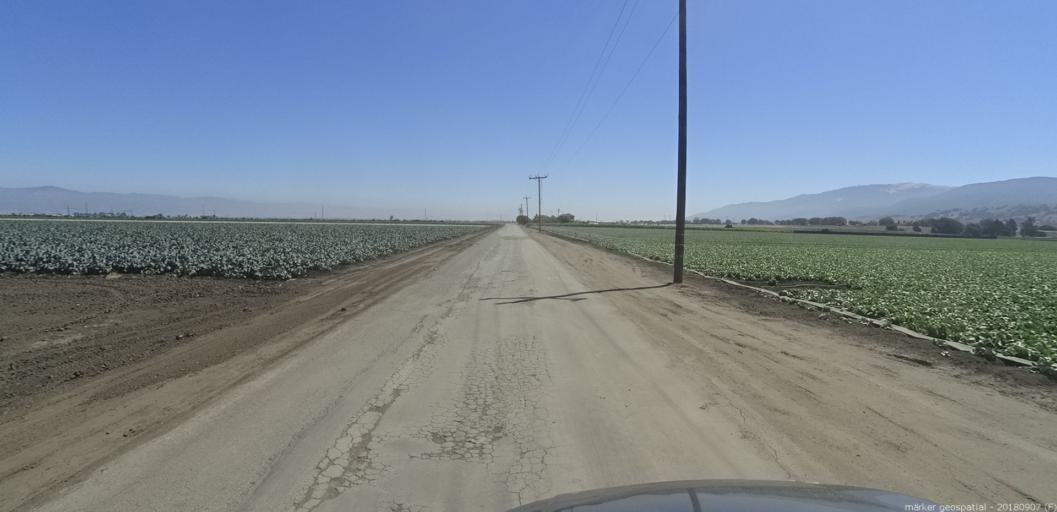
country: US
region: California
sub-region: Monterey County
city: Salinas
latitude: 36.6387
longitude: -121.6716
